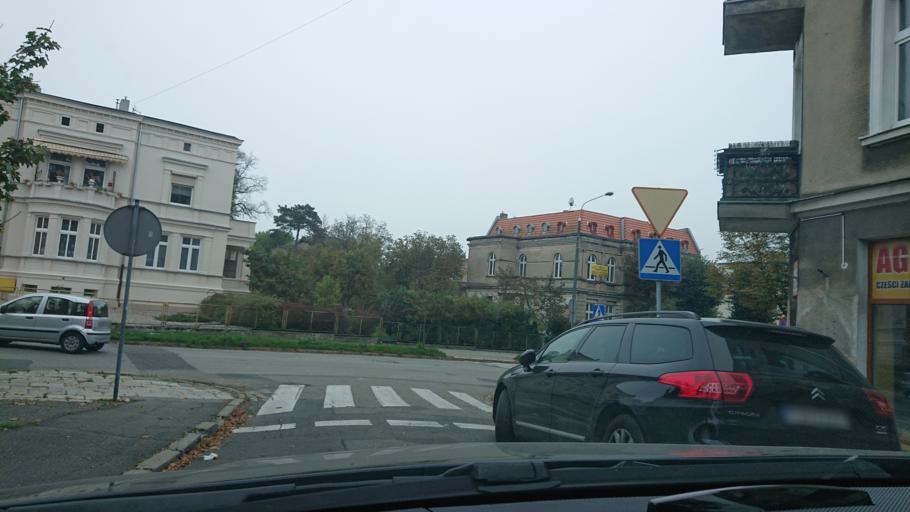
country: PL
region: Greater Poland Voivodeship
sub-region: Powiat gnieznienski
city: Gniezno
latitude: 52.5403
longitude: 17.6001
